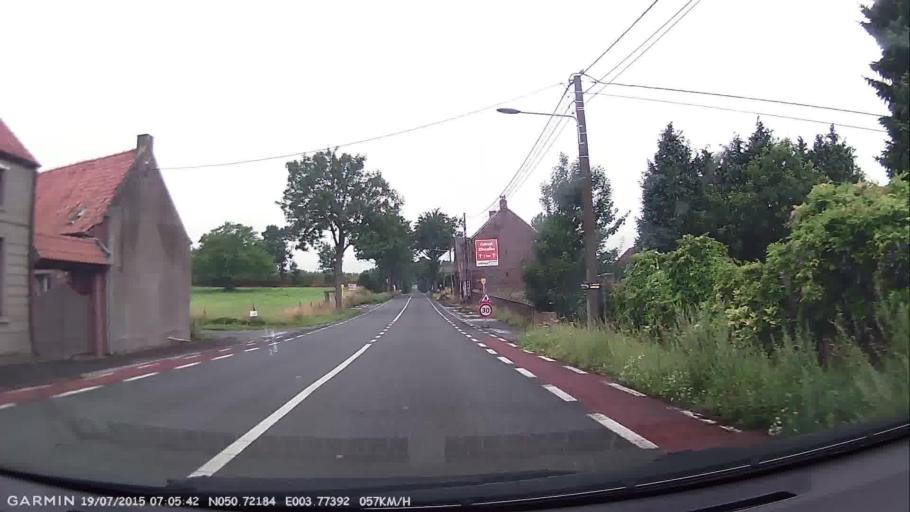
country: BE
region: Wallonia
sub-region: Province du Hainaut
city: Flobecq
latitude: 50.7219
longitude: 3.7737
